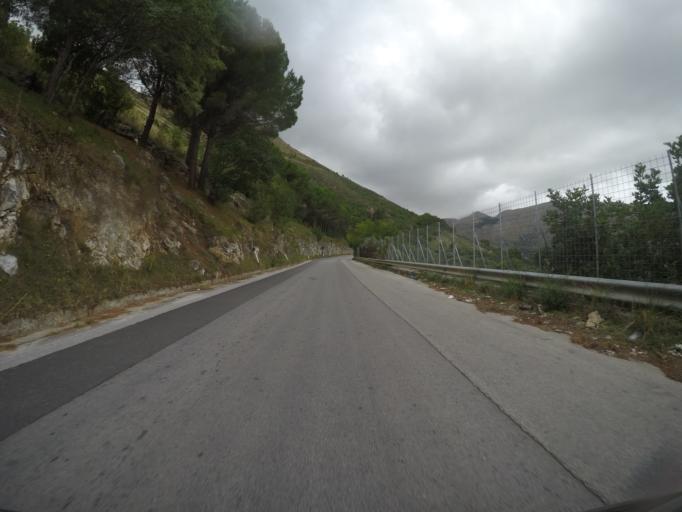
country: IT
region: Sicily
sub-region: Palermo
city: Montelepre
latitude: 38.1197
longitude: 13.1822
